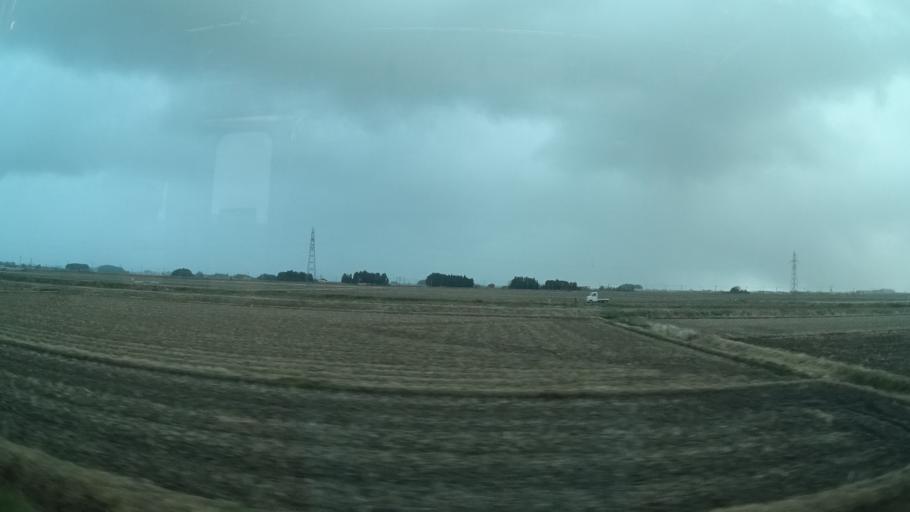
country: JP
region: Miyagi
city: Watari
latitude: 38.0537
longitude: 140.8568
